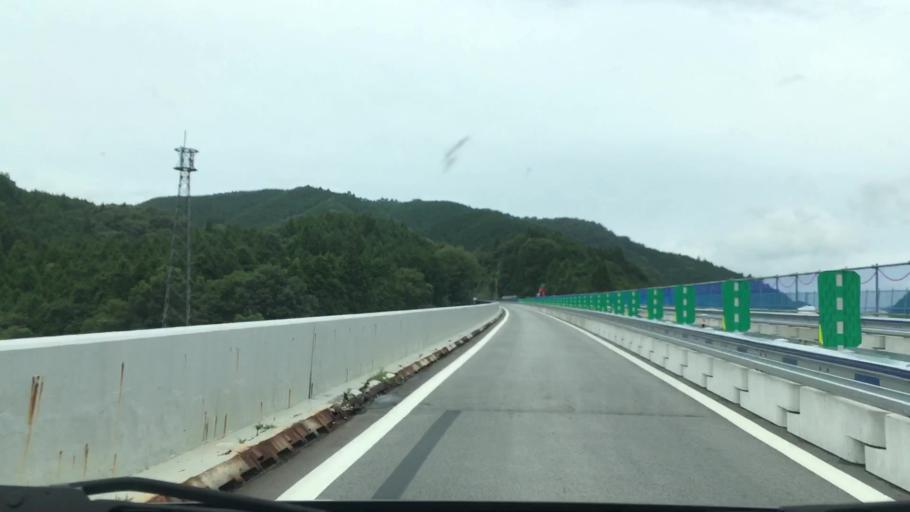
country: JP
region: Okayama
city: Niimi
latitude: 35.0303
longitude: 133.5768
